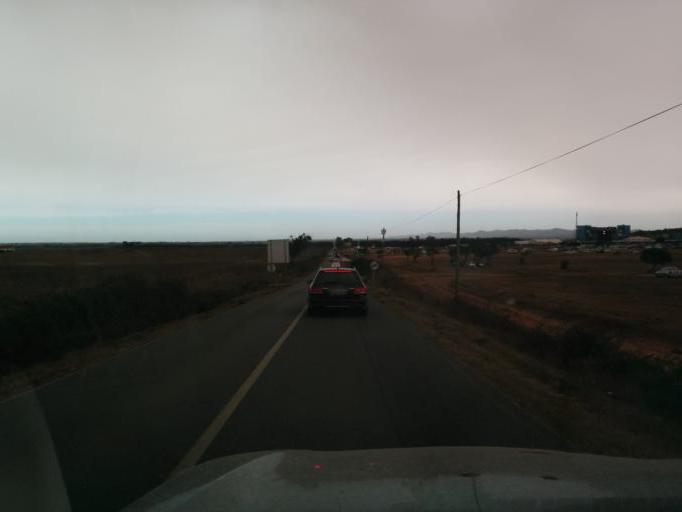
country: PT
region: Beja
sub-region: Odemira
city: Sao Teotonio
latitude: 37.5495
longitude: -8.7341
